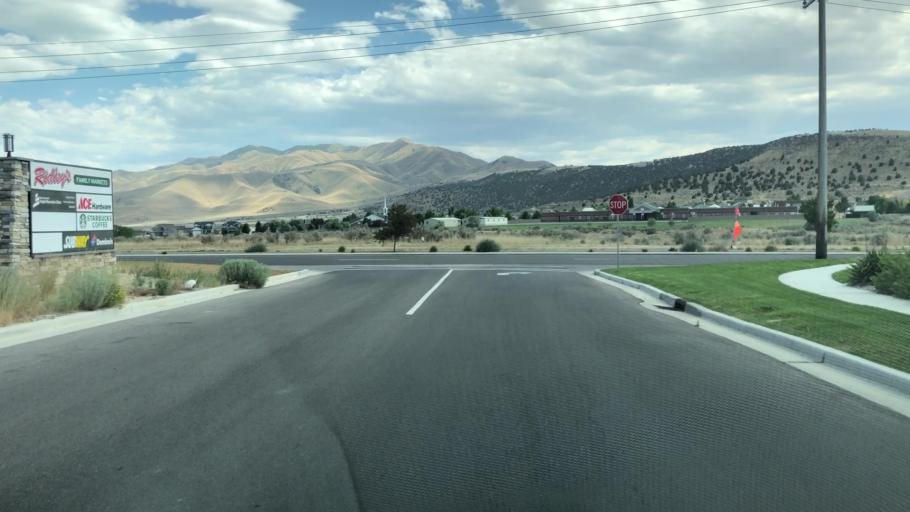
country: US
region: Utah
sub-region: Utah County
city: Saratoga Springs
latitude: 40.3626
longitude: -111.9658
